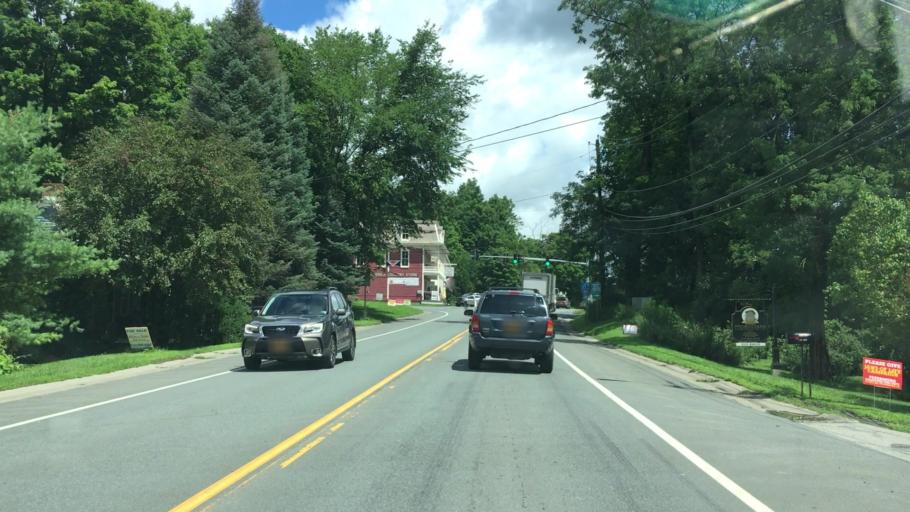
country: US
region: New York
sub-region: Rensselaer County
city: Hoosick Falls
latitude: 42.8621
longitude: -73.3291
